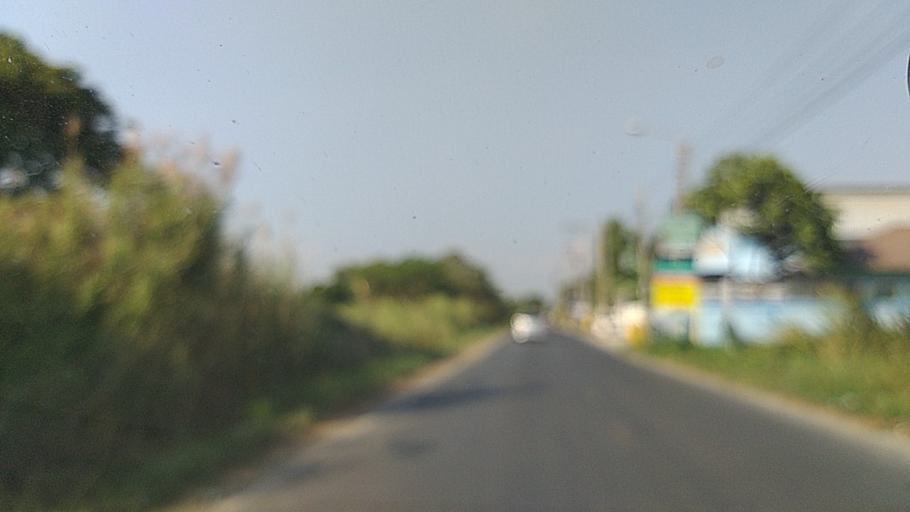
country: TH
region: Nonthaburi
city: Bang Bua Thong
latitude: 13.9384
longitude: 100.3825
